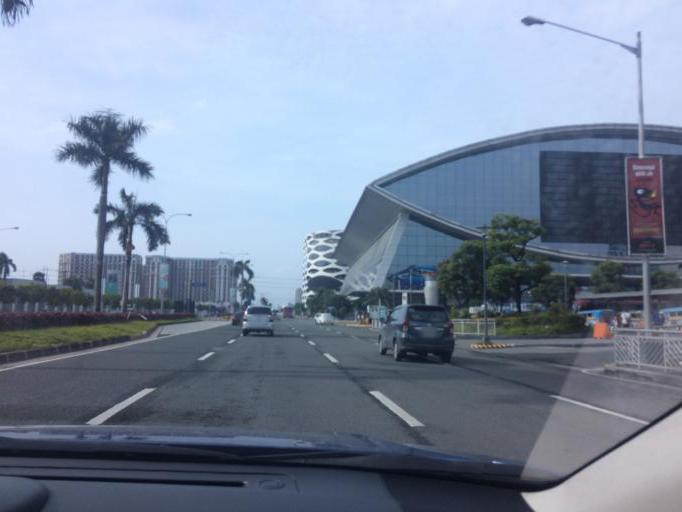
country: PH
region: Metro Manila
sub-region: Makati City
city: Makati City
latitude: 14.5341
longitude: 120.9843
